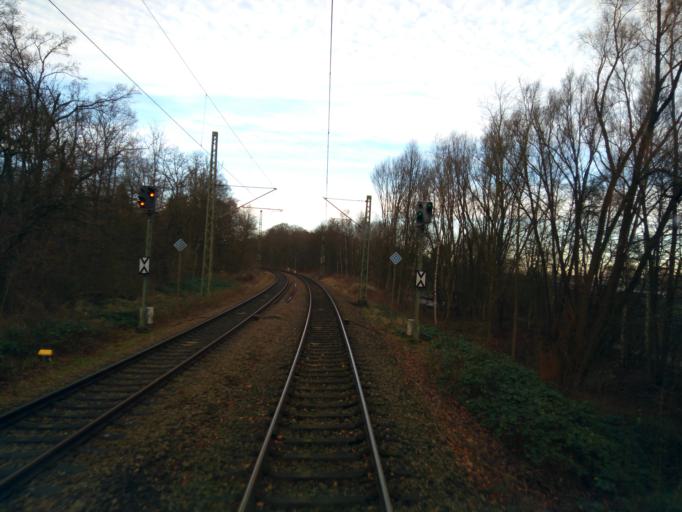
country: DE
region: Lower Saxony
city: Uelzen
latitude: 52.9773
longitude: 10.5548
